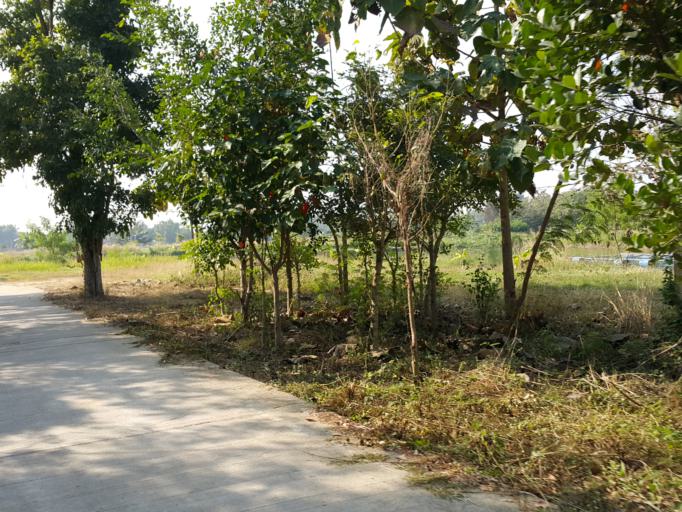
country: TH
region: Chiang Mai
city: San Kamphaeng
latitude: 18.7760
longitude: 99.0960
